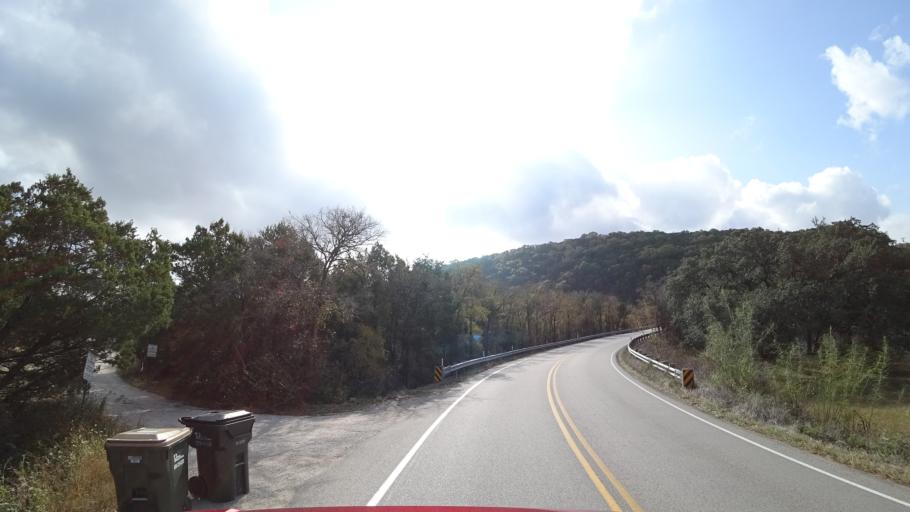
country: US
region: Texas
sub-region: Travis County
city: Hudson Bend
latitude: 30.4350
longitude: -97.8717
